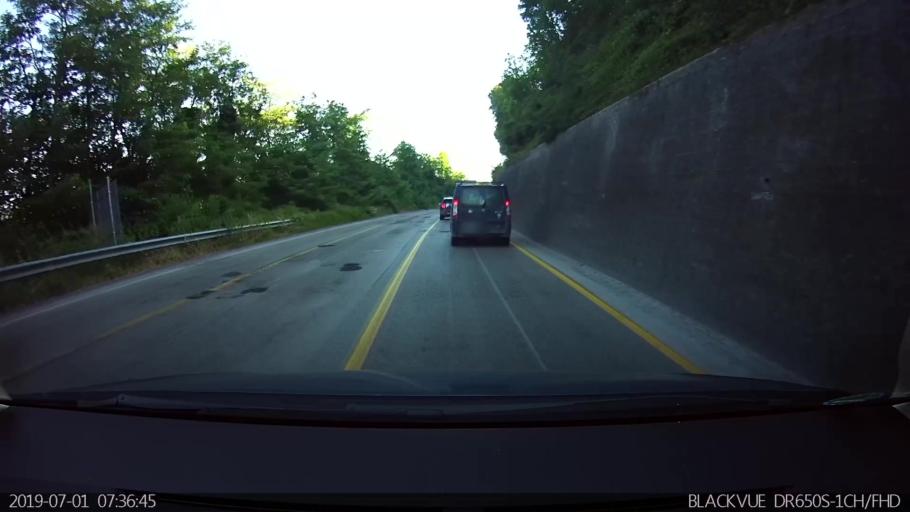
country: IT
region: Latium
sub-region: Provincia di Frosinone
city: Giuliano di Roma
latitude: 41.5334
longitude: 13.2666
